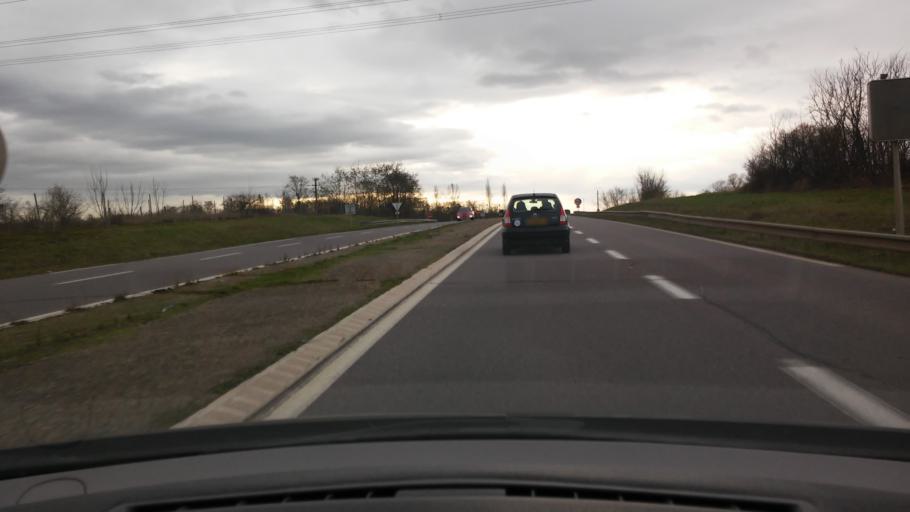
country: FR
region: Lorraine
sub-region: Departement de la Moselle
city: Argancy
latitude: 49.2005
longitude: 6.2088
